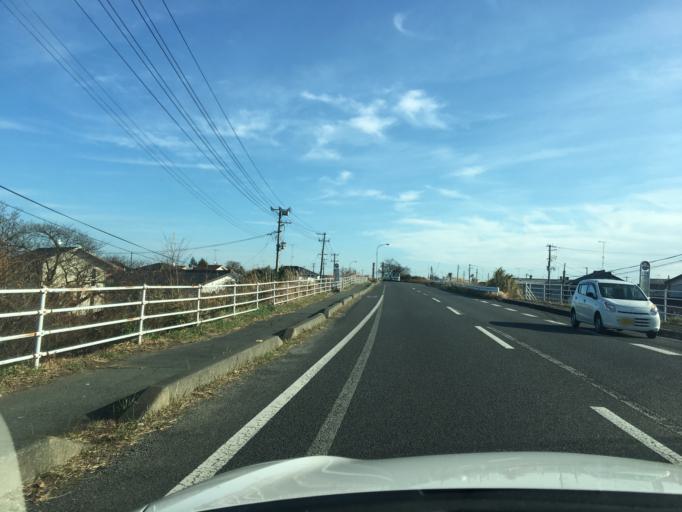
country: JP
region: Fukushima
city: Iwaki
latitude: 36.9511
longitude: 140.8786
